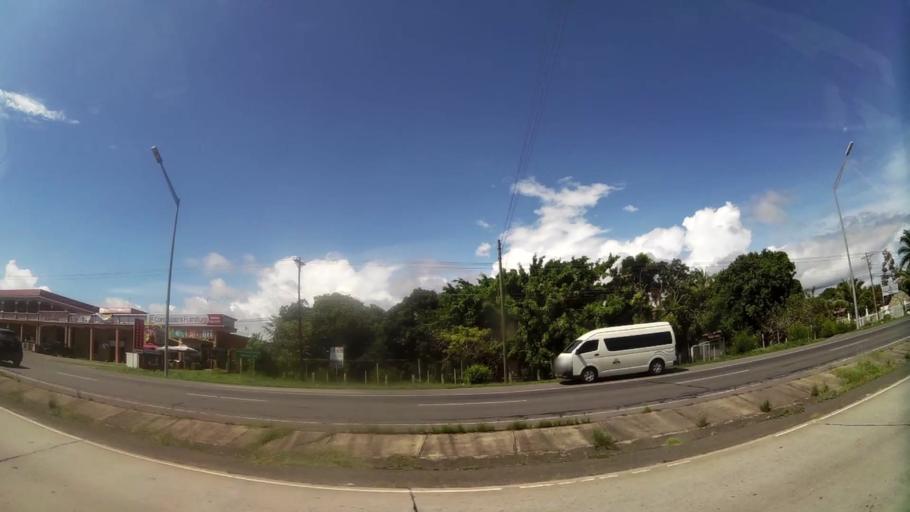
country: PA
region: Panama
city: Chame
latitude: 8.5586
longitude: -79.9033
